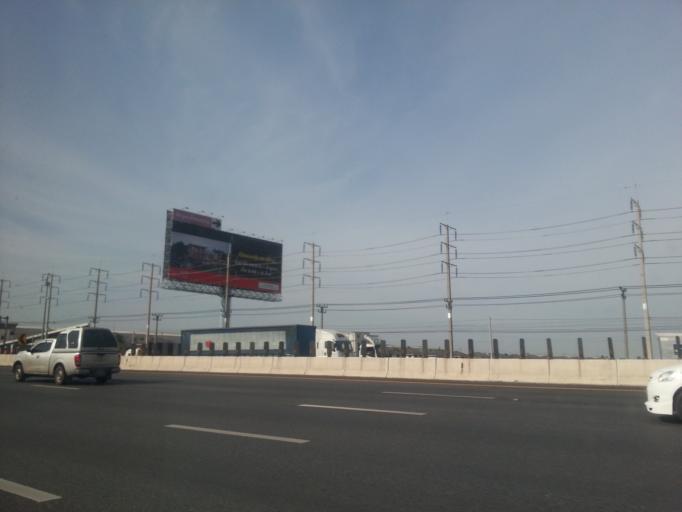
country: TH
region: Pathum Thani
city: Thanyaburi
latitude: 13.9895
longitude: 100.7126
